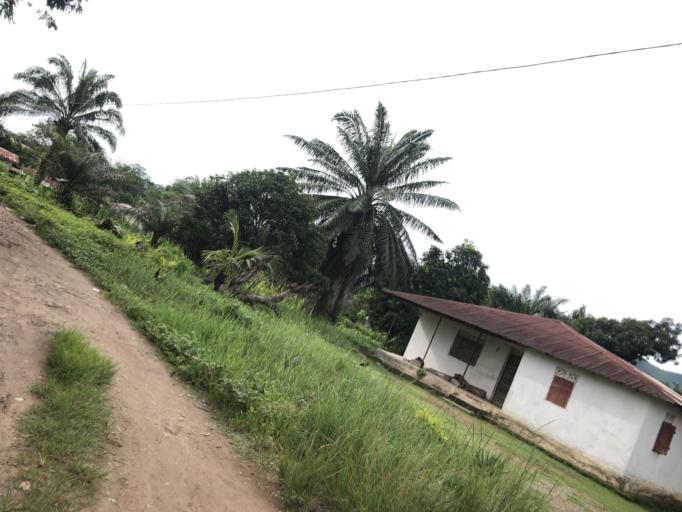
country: SL
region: Northern Province
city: Bumbuna
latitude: 9.0480
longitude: -11.7496
